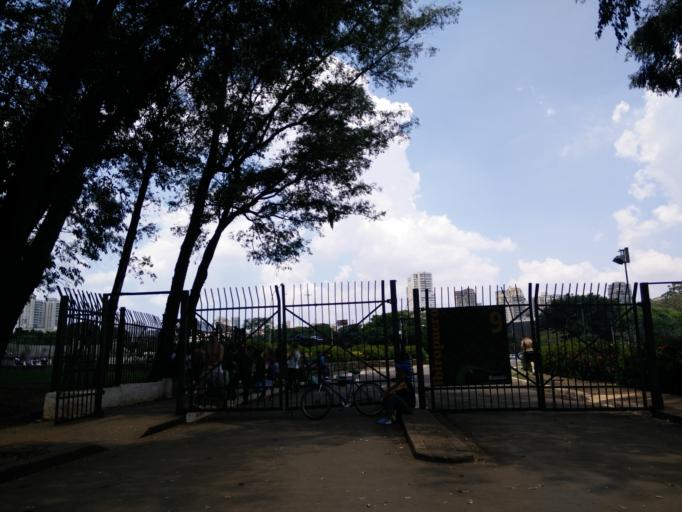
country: BR
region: Sao Paulo
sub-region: Sao Paulo
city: Sao Paulo
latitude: -23.5807
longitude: -46.6613
